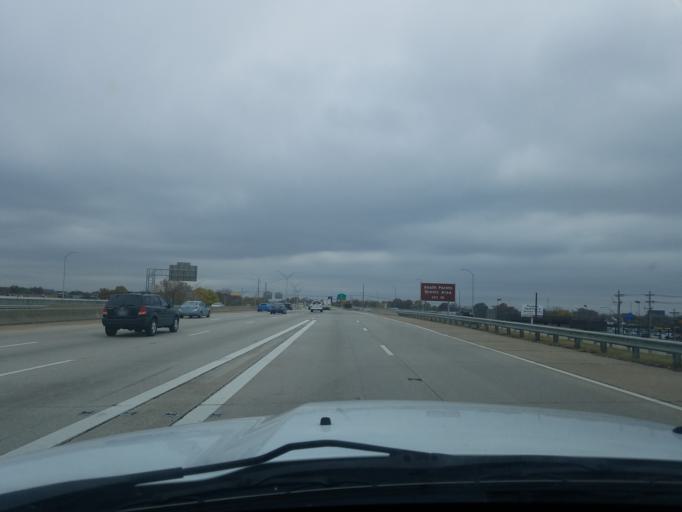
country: US
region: Kentucky
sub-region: Jefferson County
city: Audubon Park
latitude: 38.1901
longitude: -85.7498
